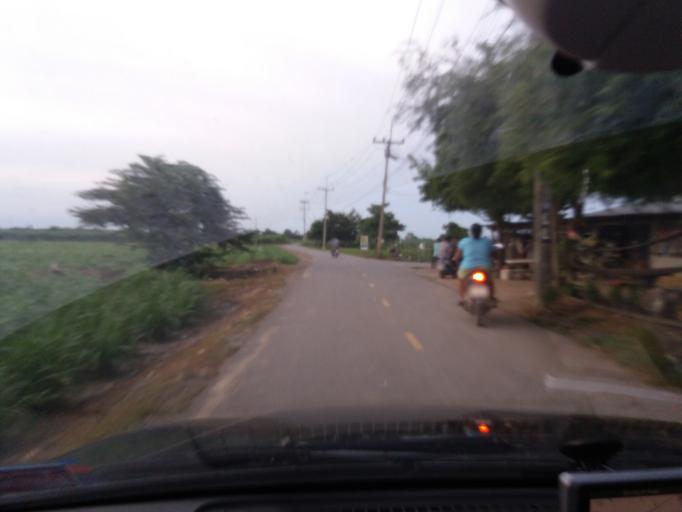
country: TH
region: Suphan Buri
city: Doembang Nangbuat
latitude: 14.8197
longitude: 100.1380
